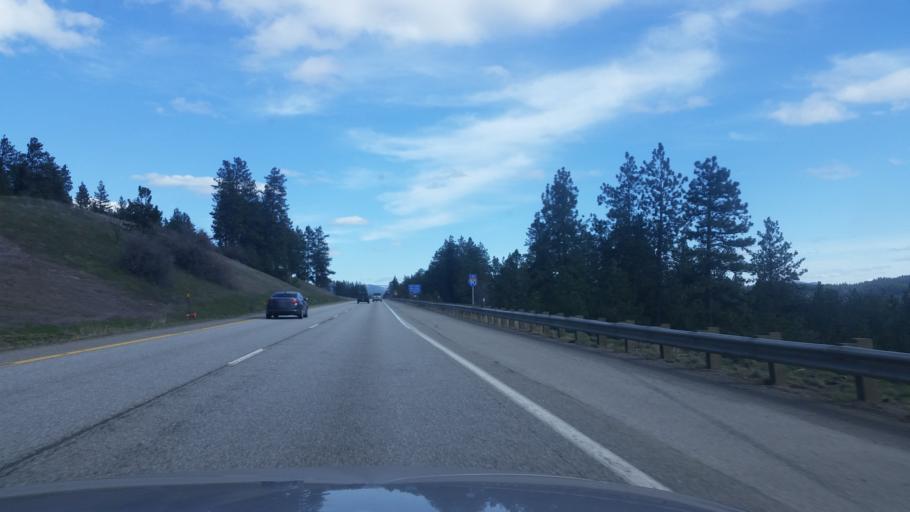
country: US
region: Idaho
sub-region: Kootenai County
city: Post Falls
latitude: 47.7089
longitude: -116.8846
